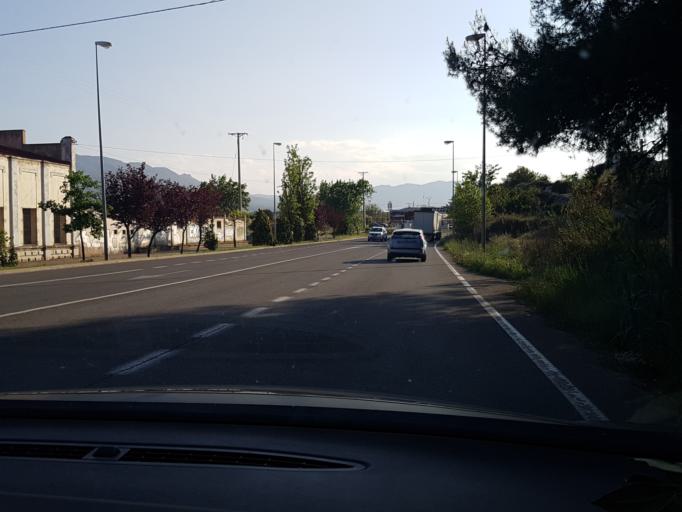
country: ES
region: La Rioja
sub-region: Provincia de La Rioja
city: Arnedo
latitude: 42.2311
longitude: -2.0833
